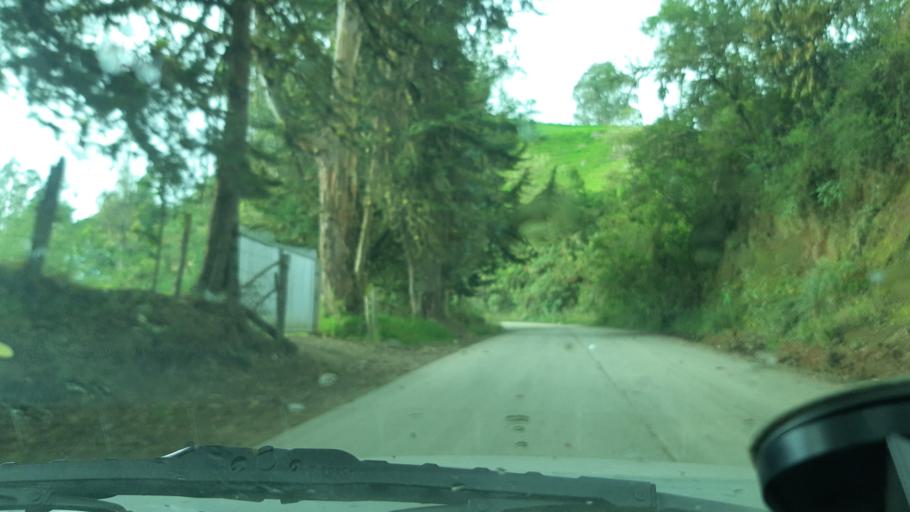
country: CO
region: Cundinamarca
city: Umbita
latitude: 5.2187
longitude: -73.4713
